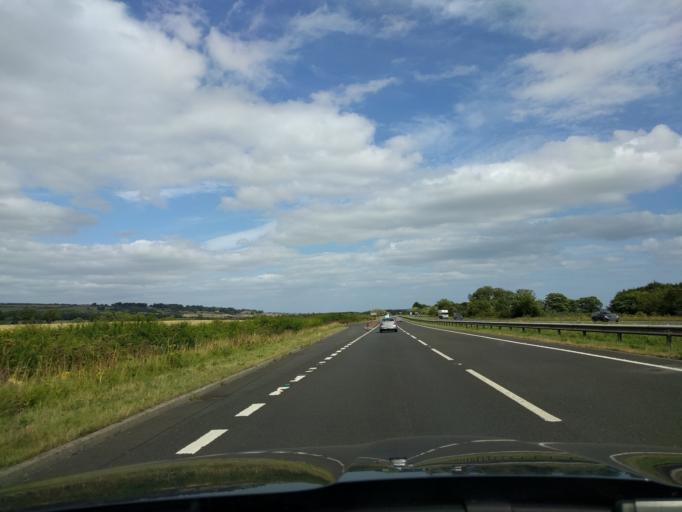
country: GB
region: England
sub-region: Northumberland
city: Alnwick
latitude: 55.3799
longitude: -1.7189
